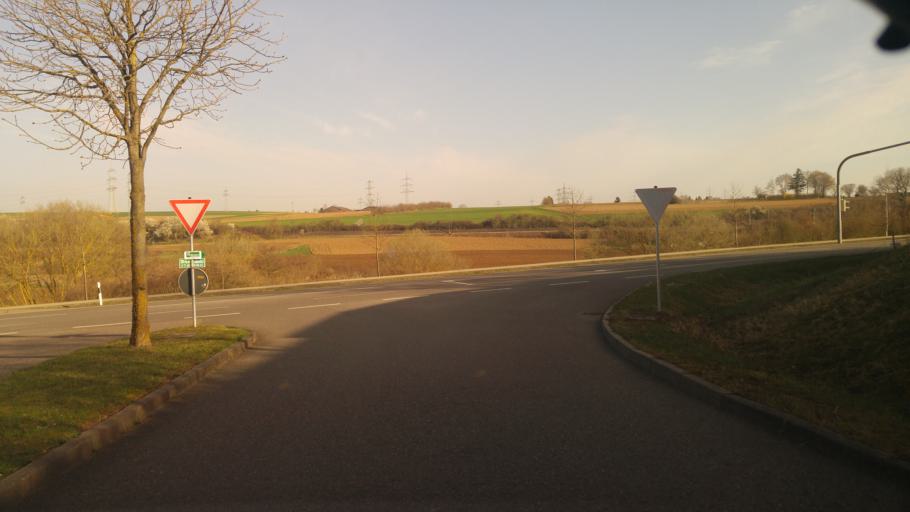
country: DE
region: Baden-Wuerttemberg
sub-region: Regierungsbezirk Stuttgart
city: Leonberg
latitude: 48.7917
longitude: 8.9896
